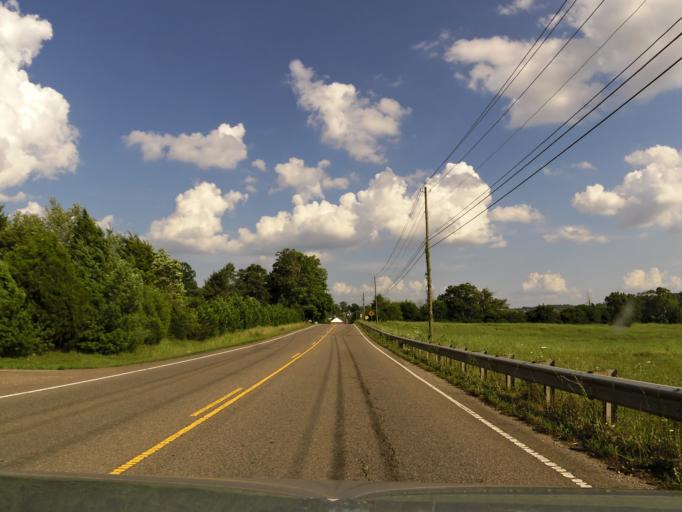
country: US
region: Tennessee
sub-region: Knox County
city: Knoxville
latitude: 36.0601
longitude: -83.8826
